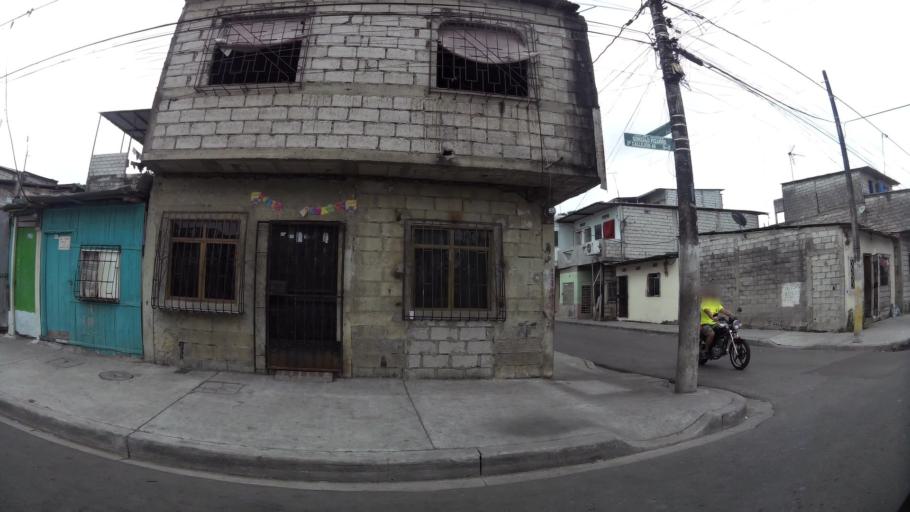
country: EC
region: Guayas
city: Guayaquil
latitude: -2.2317
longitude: -79.9120
